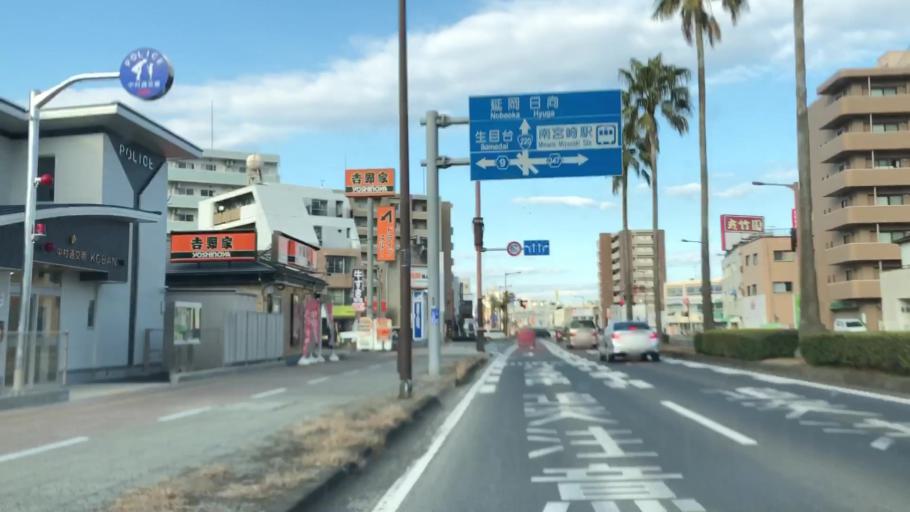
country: JP
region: Miyazaki
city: Miyazaki-shi
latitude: 31.8969
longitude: 131.4175
